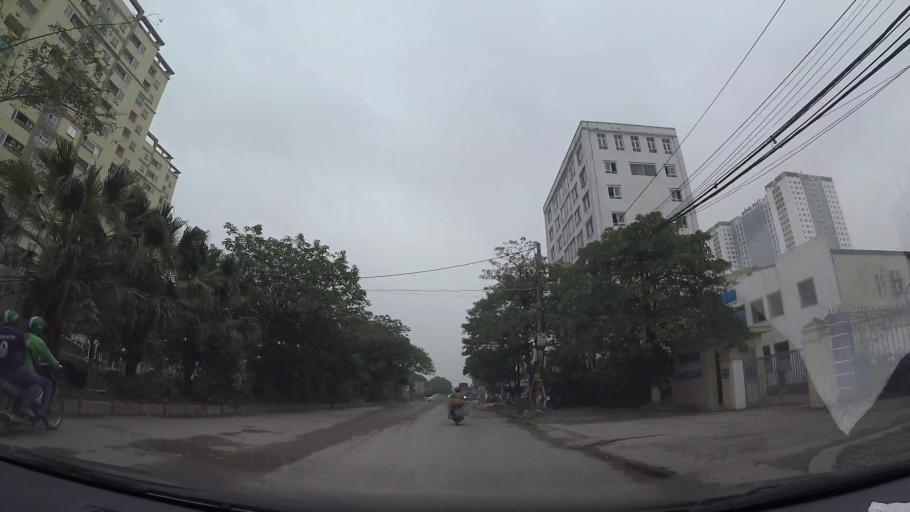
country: VN
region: Ha Noi
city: Hai BaTrung
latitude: 20.9836
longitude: 105.8692
